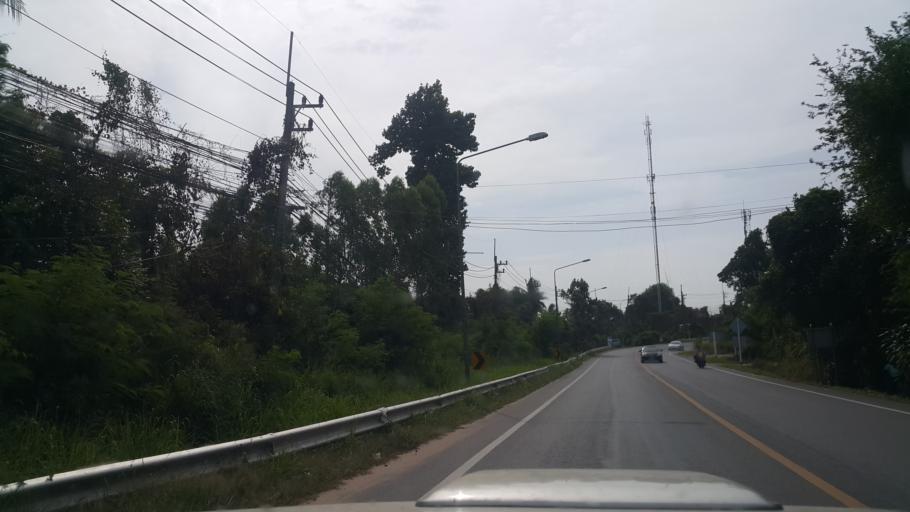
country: TH
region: Rayong
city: Ban Chang
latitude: 12.7619
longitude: 101.0198
